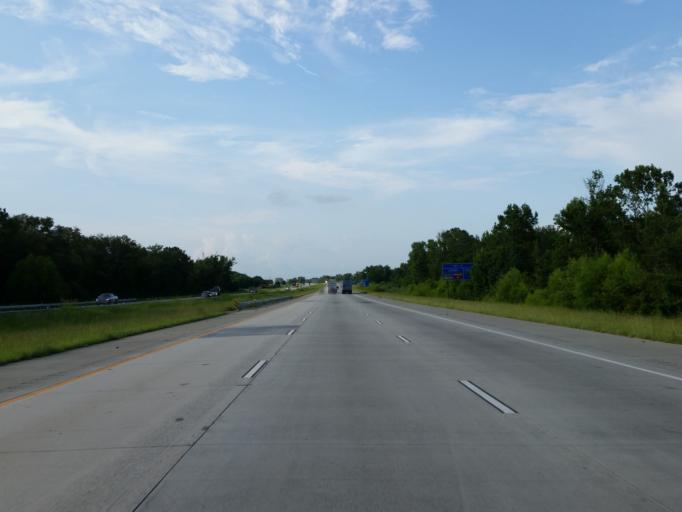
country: US
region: Georgia
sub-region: Dooly County
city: Unadilla
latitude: 32.2267
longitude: -83.7425
